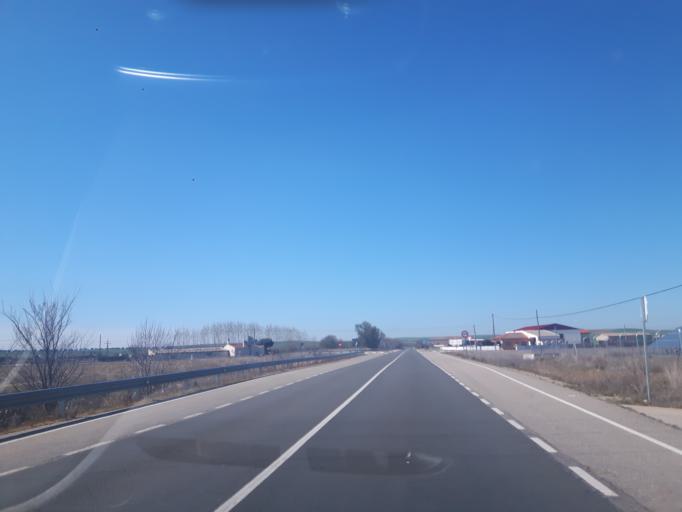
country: ES
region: Castille and Leon
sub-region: Provincia de Salamanca
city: Garcihernandez
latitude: 40.8588
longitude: -5.4278
